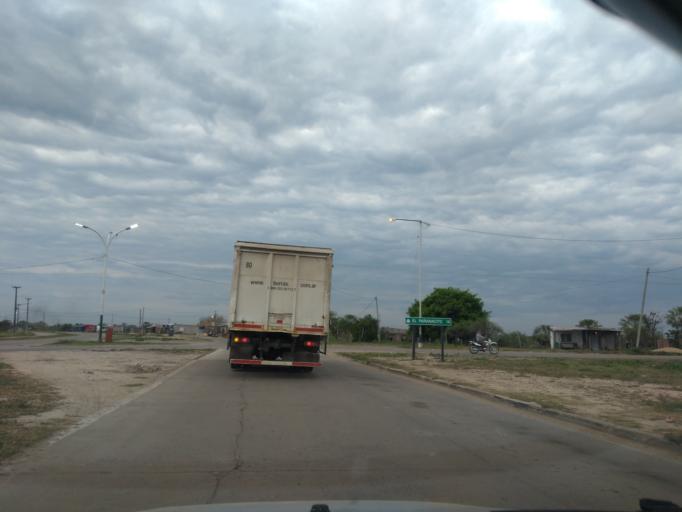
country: AR
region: Chaco
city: Puerto Vilelas
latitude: -27.5188
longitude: -58.9418
